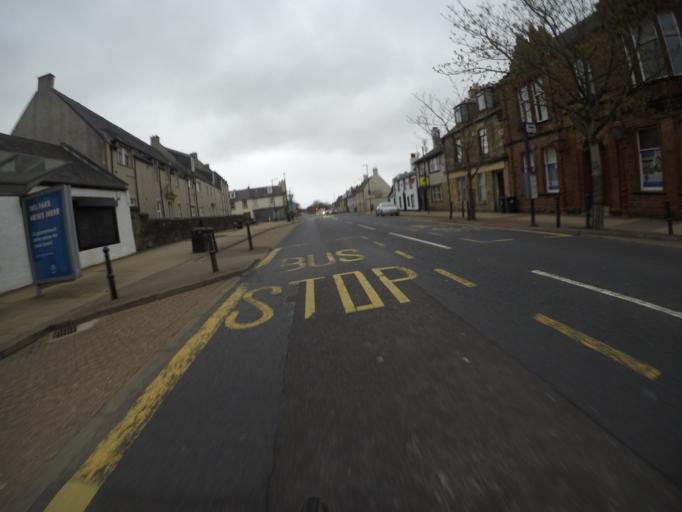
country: GB
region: Scotland
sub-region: North Ayrshire
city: Irvine
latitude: 55.6173
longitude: -4.6689
